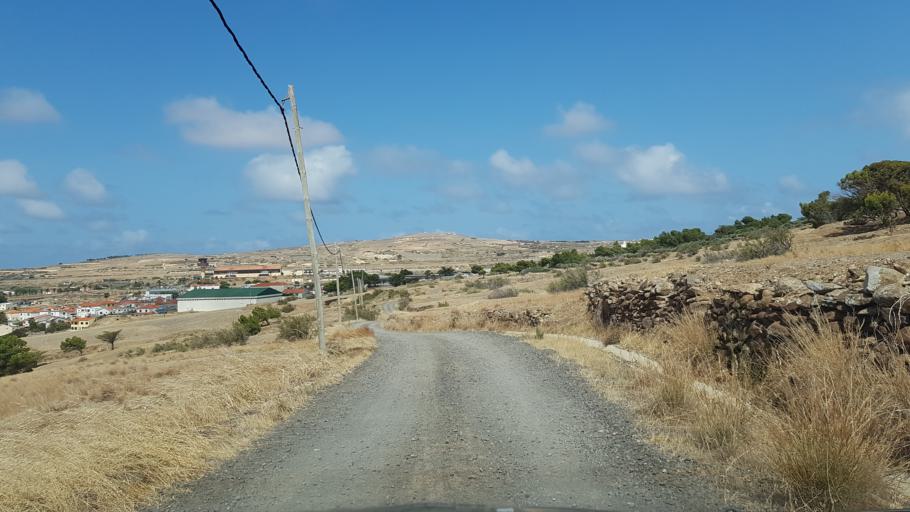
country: PT
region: Madeira
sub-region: Porto Santo
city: Vila de Porto Santo
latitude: 33.0716
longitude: -16.3335
